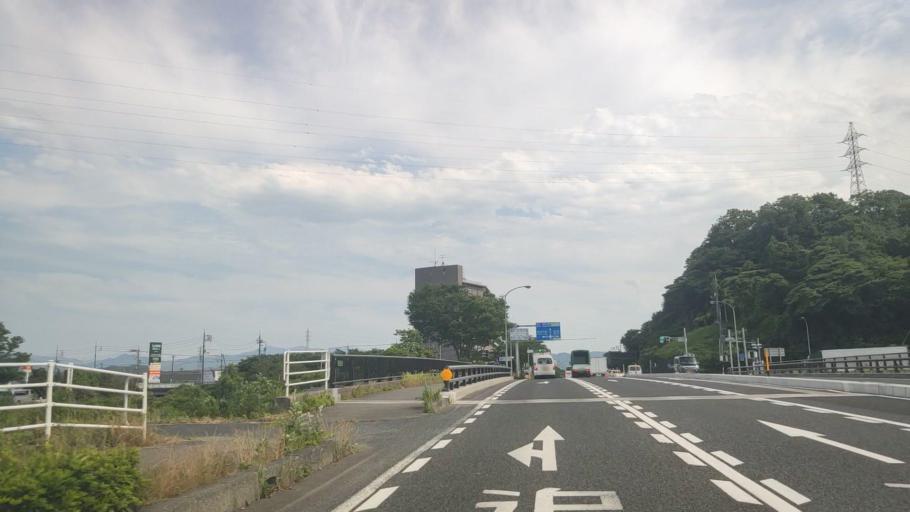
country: JP
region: Tottori
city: Tottori
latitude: 35.4997
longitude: 134.2019
